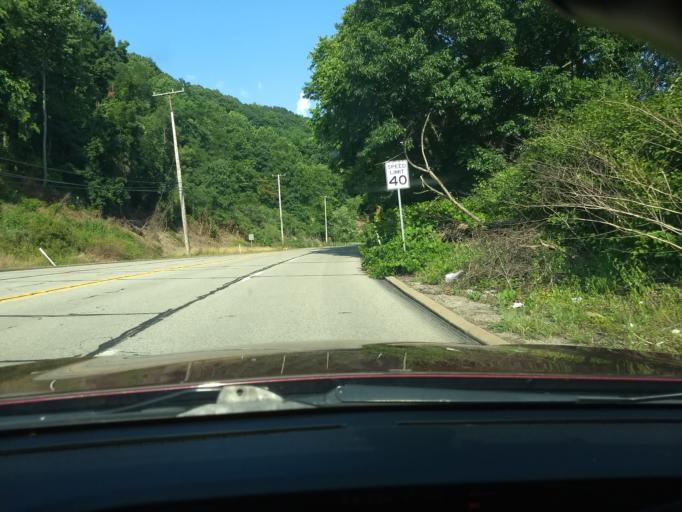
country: US
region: Pennsylvania
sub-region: Allegheny County
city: Versailles
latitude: 40.3246
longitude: -79.8345
